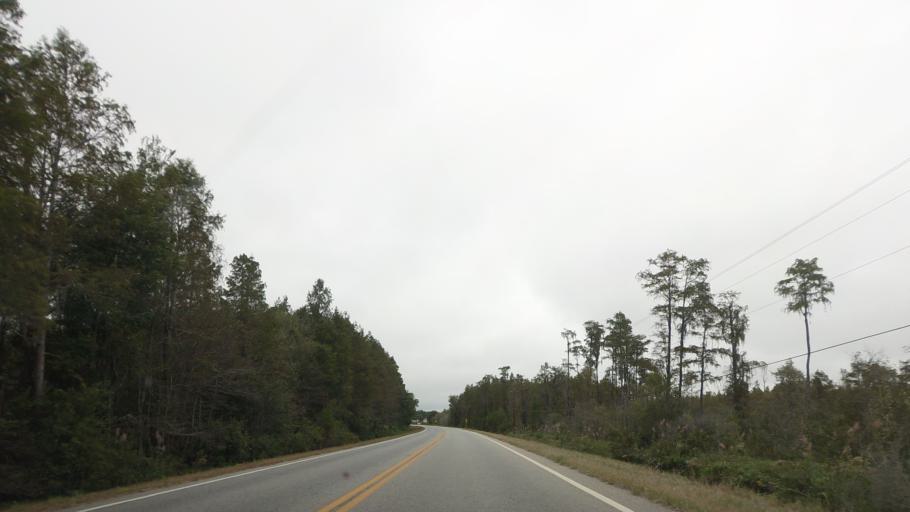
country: US
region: Georgia
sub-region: Berrien County
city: Nashville
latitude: 31.1765
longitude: -83.2344
